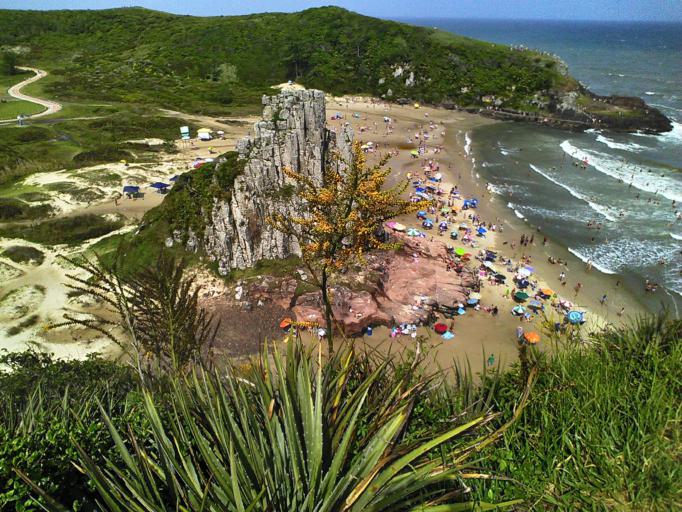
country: BR
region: Rio Grande do Sul
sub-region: Torres
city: Torres
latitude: -29.3581
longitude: -49.7351
